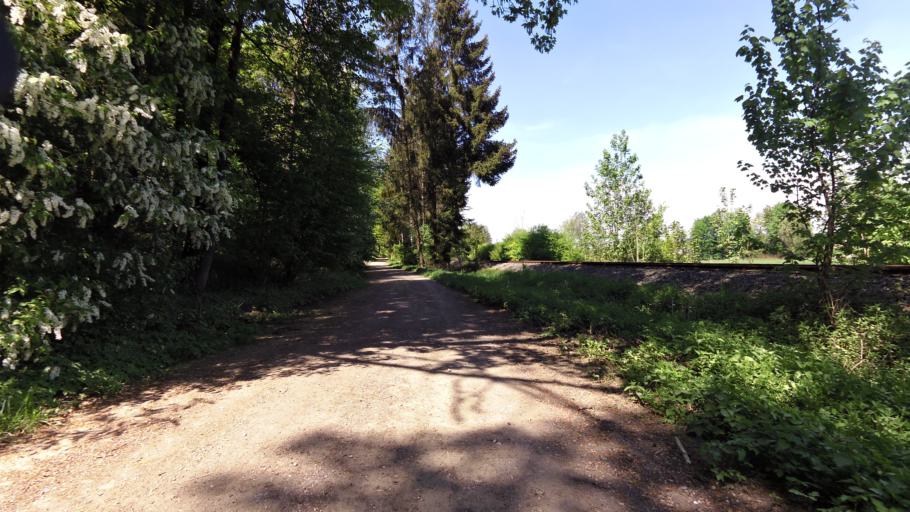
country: DE
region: Bavaria
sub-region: Lower Bavaria
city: Weihmichl
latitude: 48.5647
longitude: 12.0848
